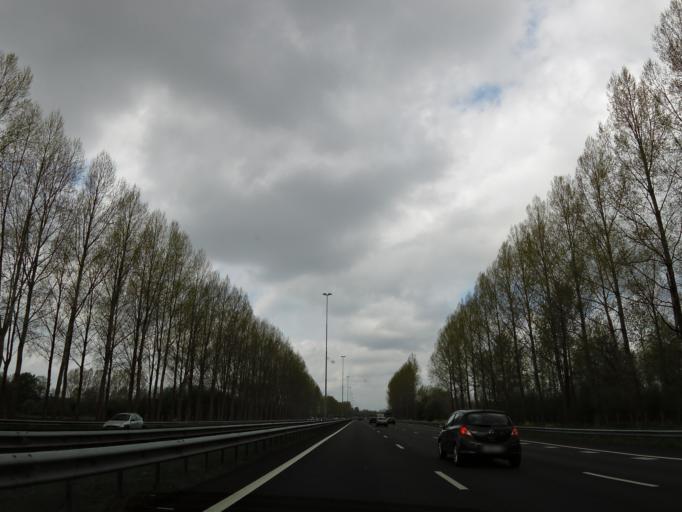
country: NL
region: North Brabant
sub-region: Gemeente Best
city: Best
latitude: 51.5511
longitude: 5.3654
